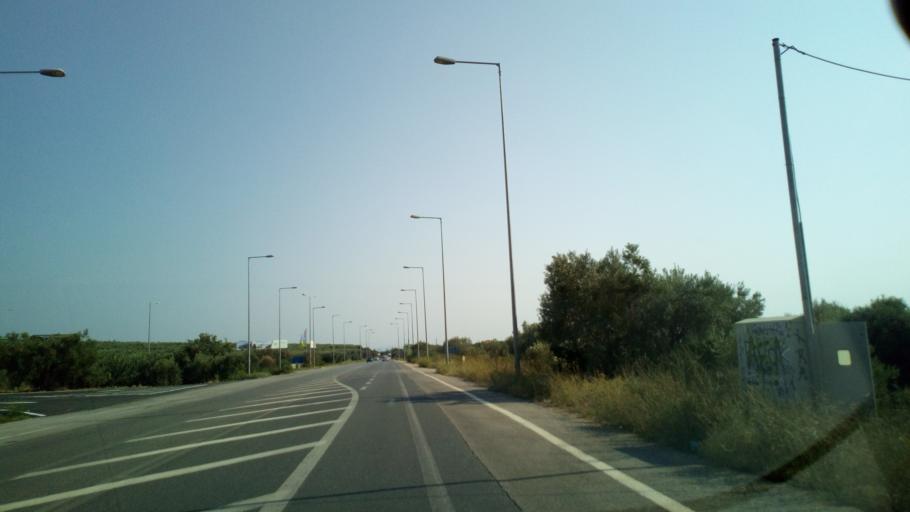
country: GR
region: Central Macedonia
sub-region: Nomos Chalkidikis
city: Kalyves Polygyrou
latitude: 40.2851
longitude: 23.4307
